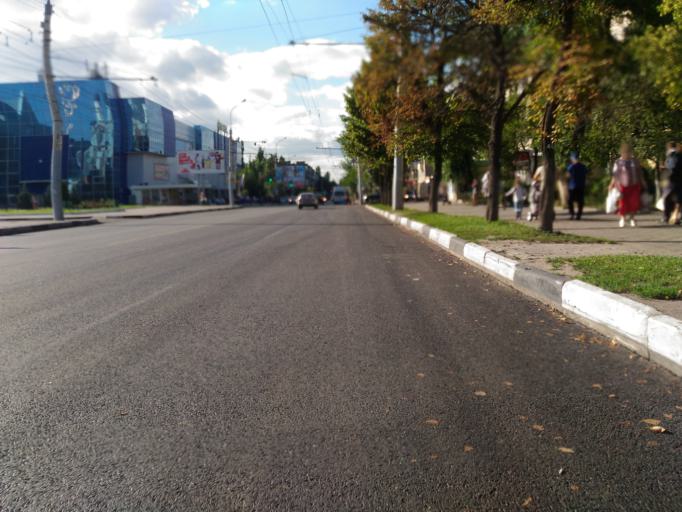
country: RU
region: Voronezj
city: Voronezh
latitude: 51.6520
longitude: 39.1507
